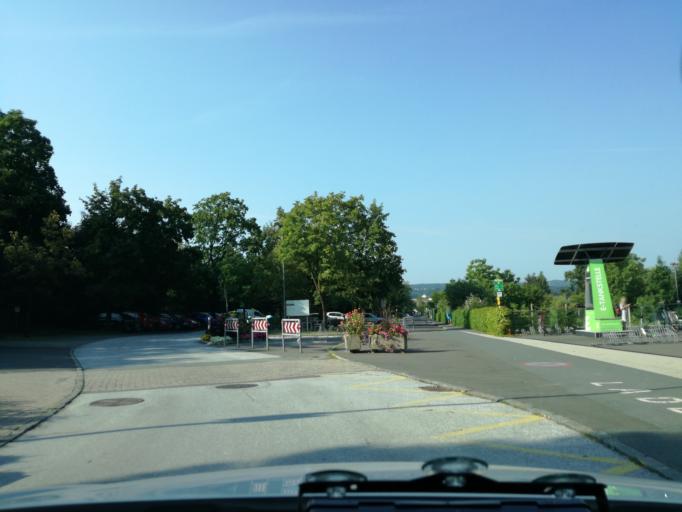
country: AT
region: Styria
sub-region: Politischer Bezirk Weiz
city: Gleisdorf
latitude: 47.1114
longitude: 15.7114
